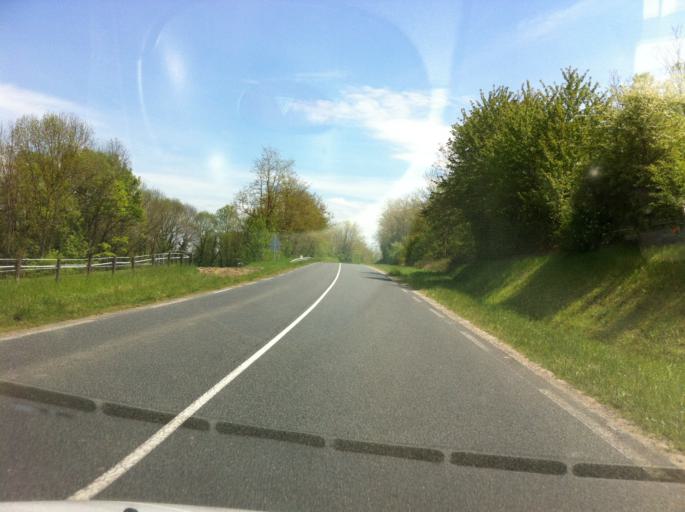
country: FR
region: Auvergne
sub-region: Departement de l'Allier
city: Saint-Pourcain-sur-Sioule
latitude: 46.3174
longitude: 3.2484
